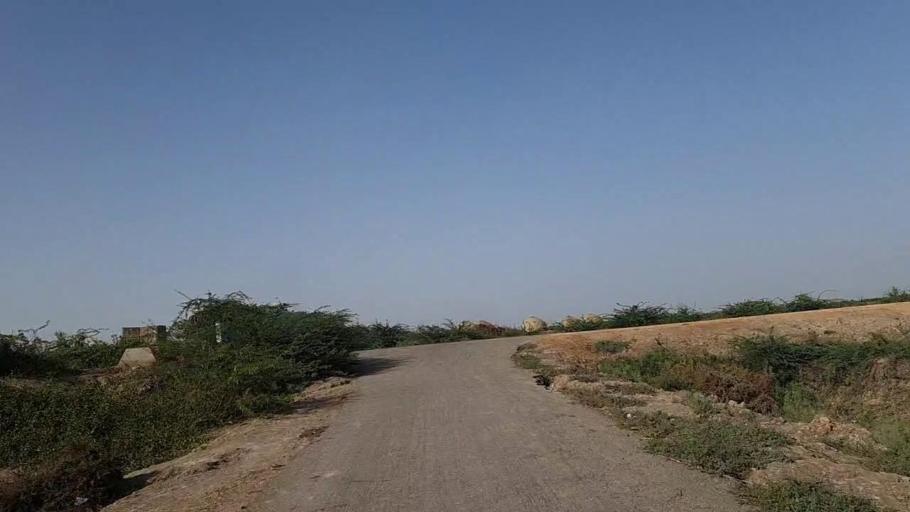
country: PK
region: Sindh
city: Jati
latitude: 24.3076
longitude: 68.1968
